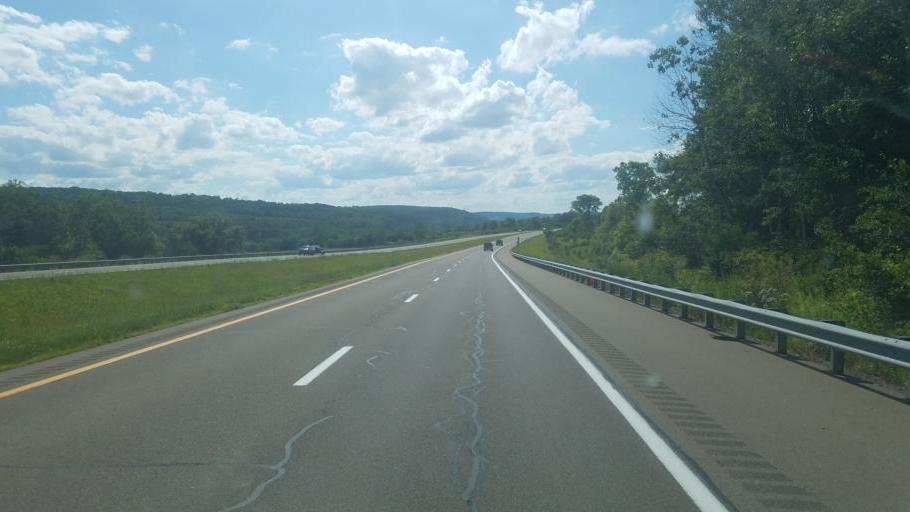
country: US
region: New York
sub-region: Steuben County
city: Hornell
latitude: 42.3681
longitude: -77.6125
